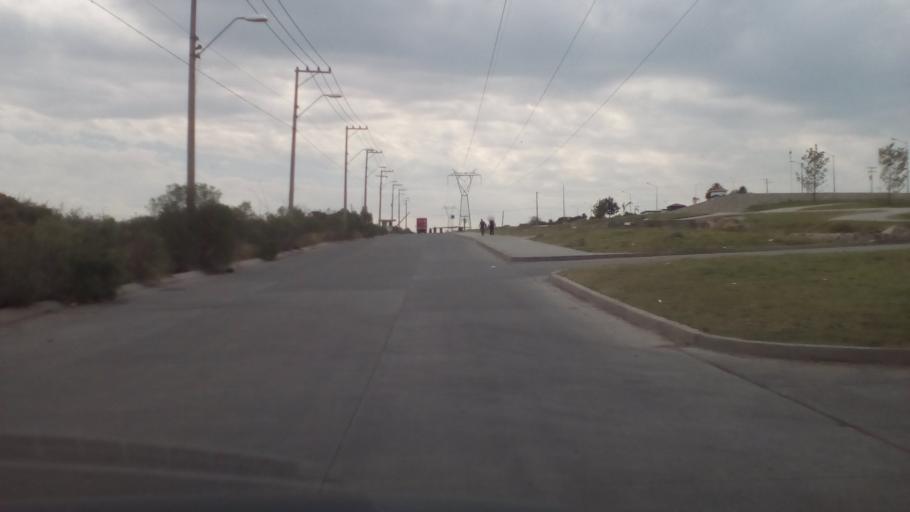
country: MX
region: Guanajuato
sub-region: Leon
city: Fraccionamiento Paseo de las Torres
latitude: 21.1728
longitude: -101.7635
